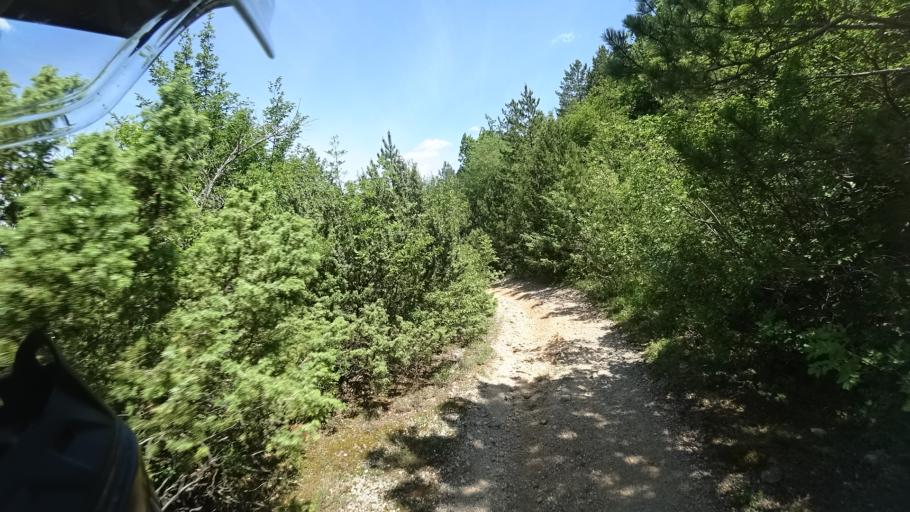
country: HR
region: Sibensko-Kniniska
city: Knin
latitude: 44.0336
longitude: 16.2299
